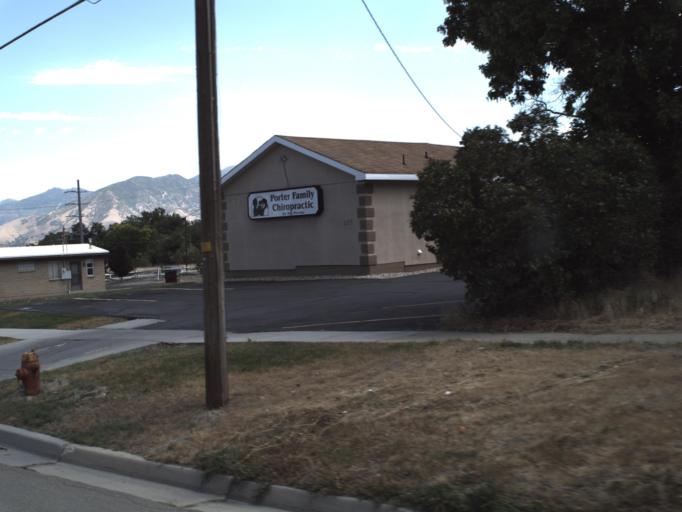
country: US
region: Utah
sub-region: Tooele County
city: Tooele
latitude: 40.5218
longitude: -112.2987
